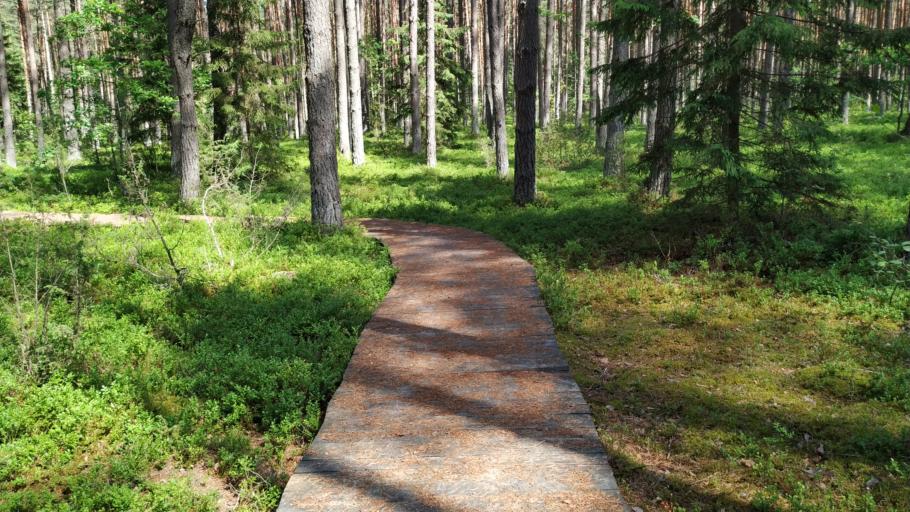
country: LT
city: Nemencine
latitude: 54.8090
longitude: 25.3975
